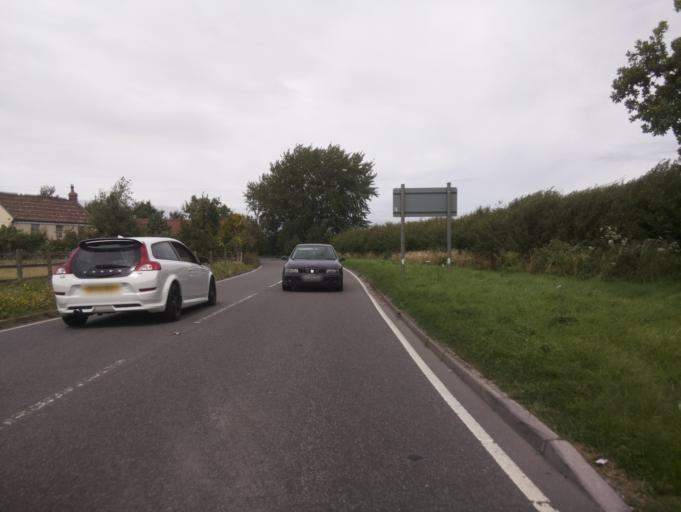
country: GB
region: England
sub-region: North Somerset
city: Kenn
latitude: 51.4029
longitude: -2.8422
